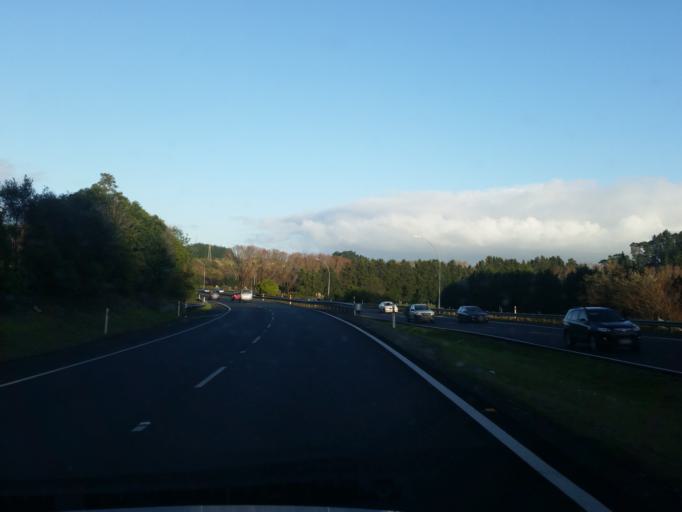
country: NZ
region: Auckland
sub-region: Auckland
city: Pukekohe East
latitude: -37.2601
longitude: 175.0399
